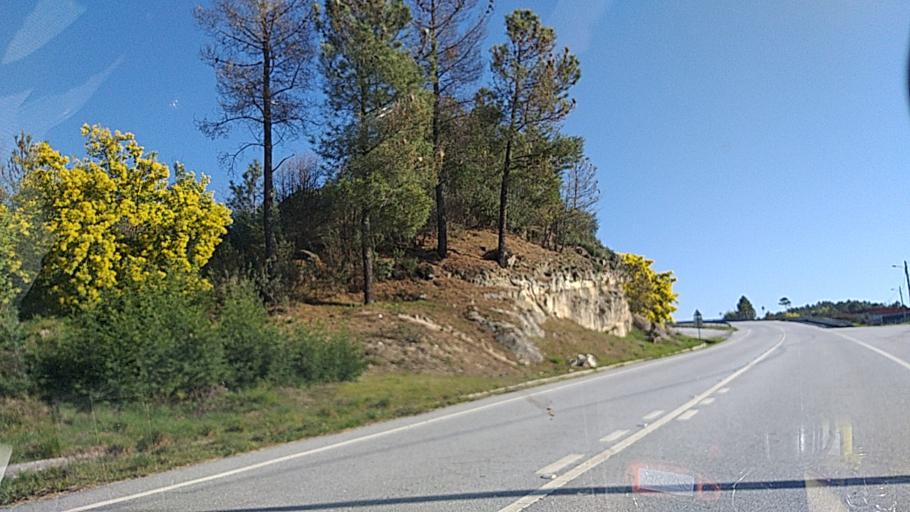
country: PT
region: Guarda
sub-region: Fornos de Algodres
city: Fornos de Algodres
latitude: 40.6171
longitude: -7.5137
